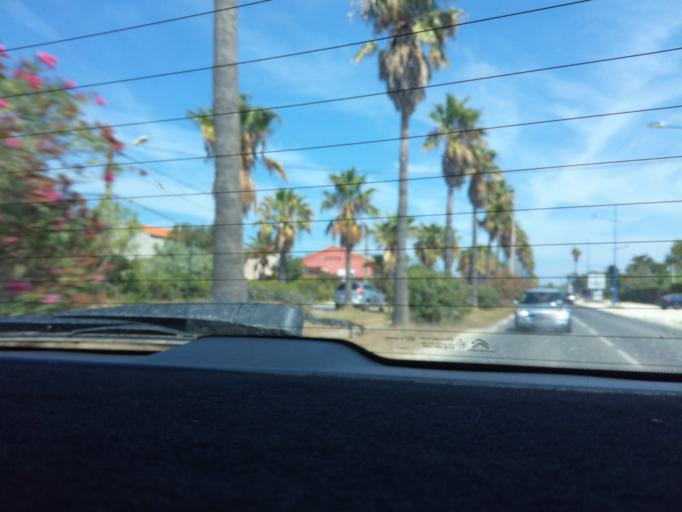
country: FR
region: Provence-Alpes-Cote d'Azur
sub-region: Departement du Var
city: Hyeres
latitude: 43.0447
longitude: 6.1459
